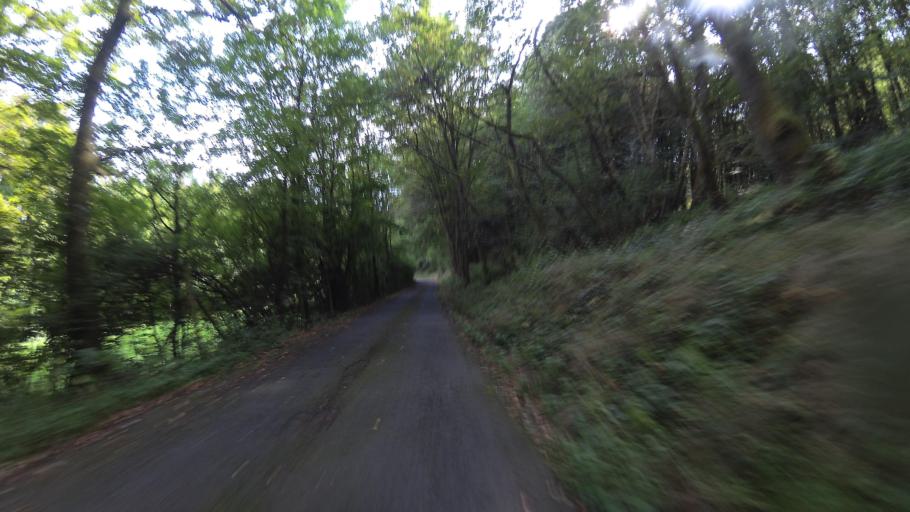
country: DE
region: Rheinland-Pfalz
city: Herchweiler
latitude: 49.4971
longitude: 7.2435
